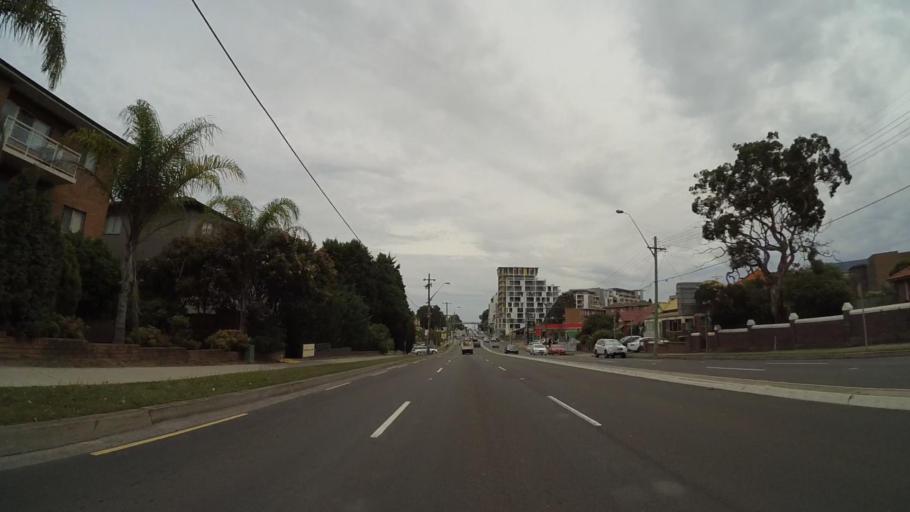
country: AU
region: New South Wales
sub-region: Rockdale
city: Brighton-Le-Sands
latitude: -33.9624
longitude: 151.1376
